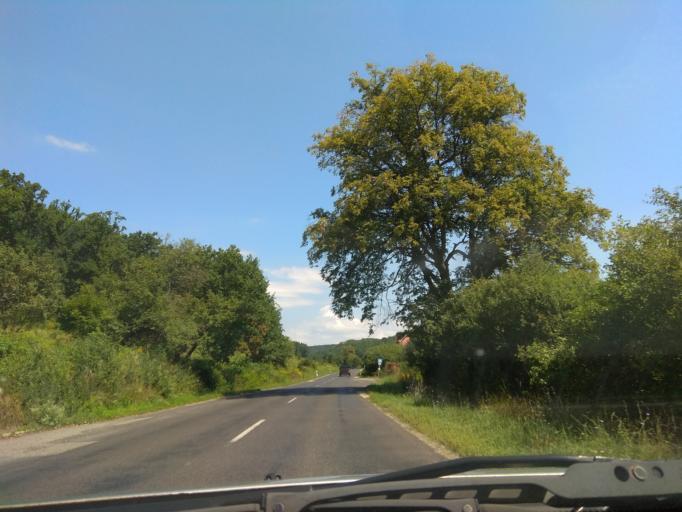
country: HU
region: Borsod-Abauj-Zemplen
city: Harsany
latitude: 48.0035
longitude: 20.7606
